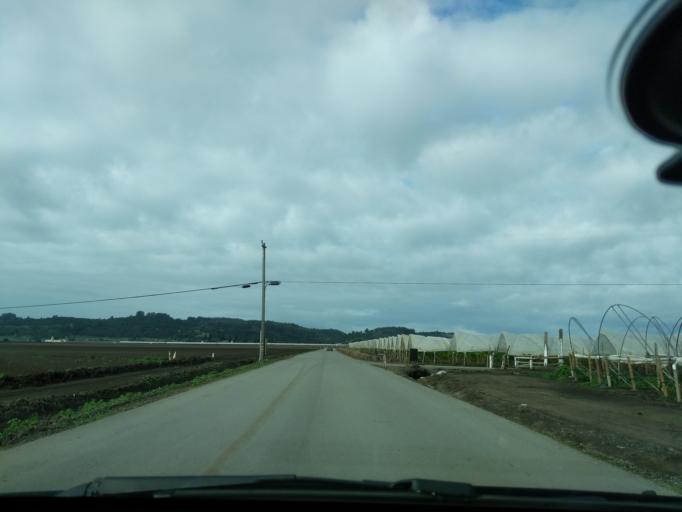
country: US
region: California
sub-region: San Benito County
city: Aromas
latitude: 36.9044
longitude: -121.6669
